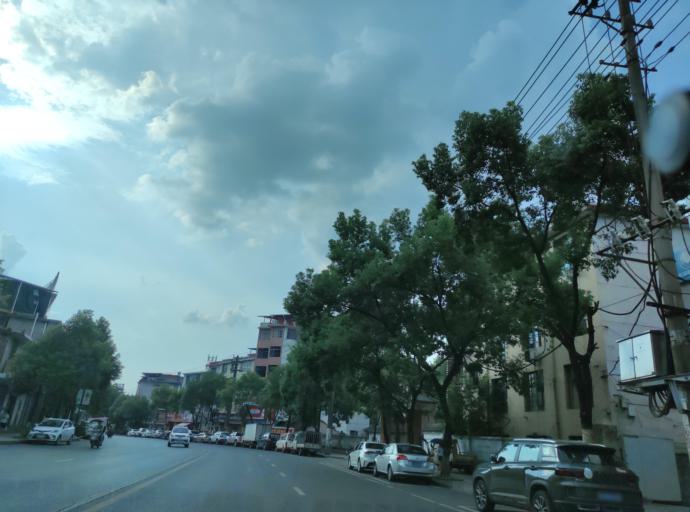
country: CN
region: Jiangxi Sheng
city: Pingxiang
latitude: 27.6612
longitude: 113.8380
